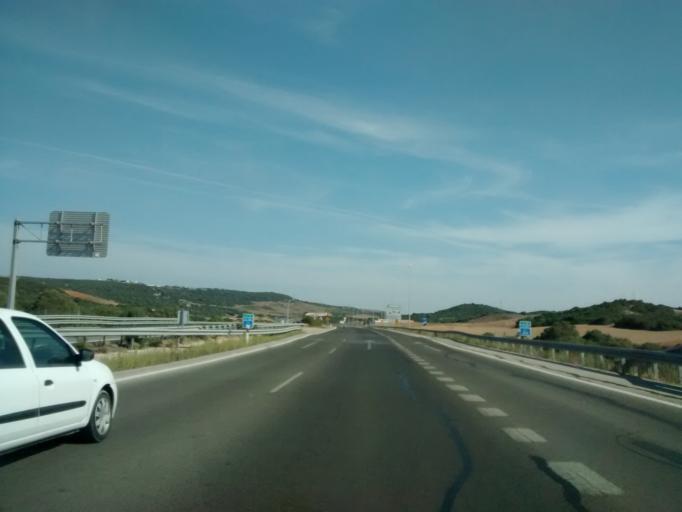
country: ES
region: Andalusia
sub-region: Provincia de Cadiz
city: Conil de la Frontera
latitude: 36.3030
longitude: -6.0559
